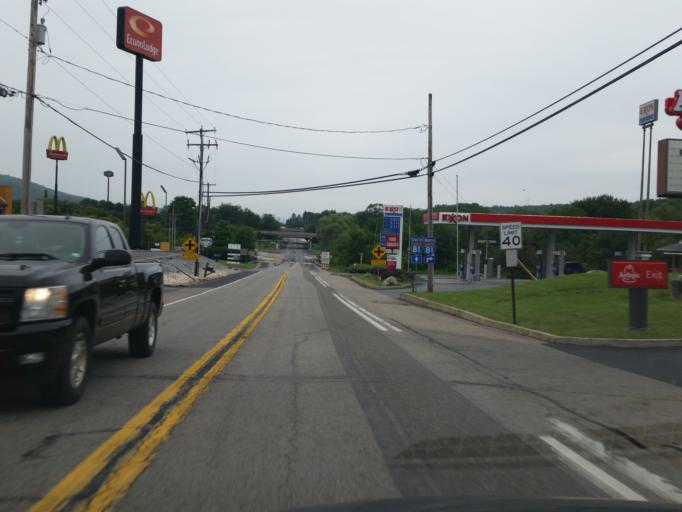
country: US
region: Pennsylvania
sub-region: Schuylkill County
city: Pine Grove
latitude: 40.5353
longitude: -76.4249
